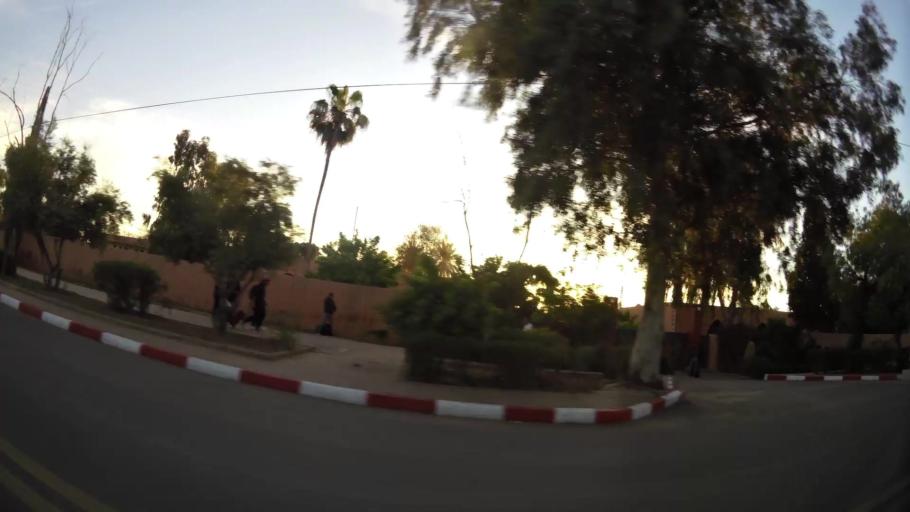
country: MA
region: Marrakech-Tensift-Al Haouz
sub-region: Marrakech
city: Marrakesh
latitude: 31.6378
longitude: -8.0312
